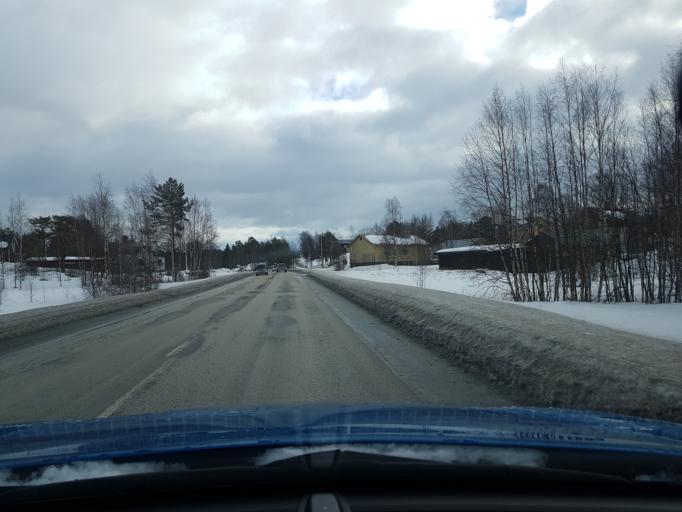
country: SE
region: Jaemtland
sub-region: Harjedalens Kommun
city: Sveg
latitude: 62.4100
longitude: 13.6848
